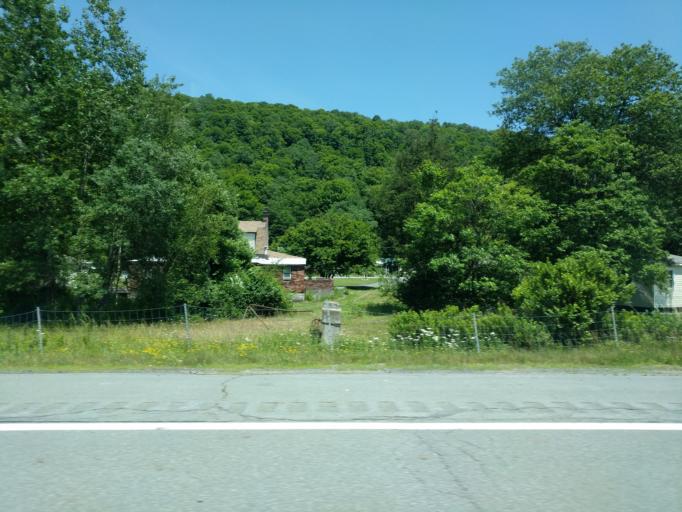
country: US
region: New York
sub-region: Sullivan County
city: Livingston Manor
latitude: 41.8676
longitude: -74.7905
